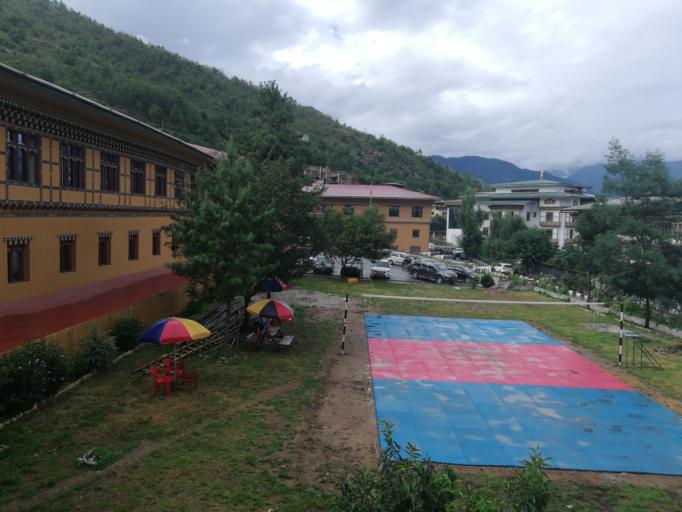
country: BT
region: Thimphu
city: Thimphu
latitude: 27.4801
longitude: 89.6306
